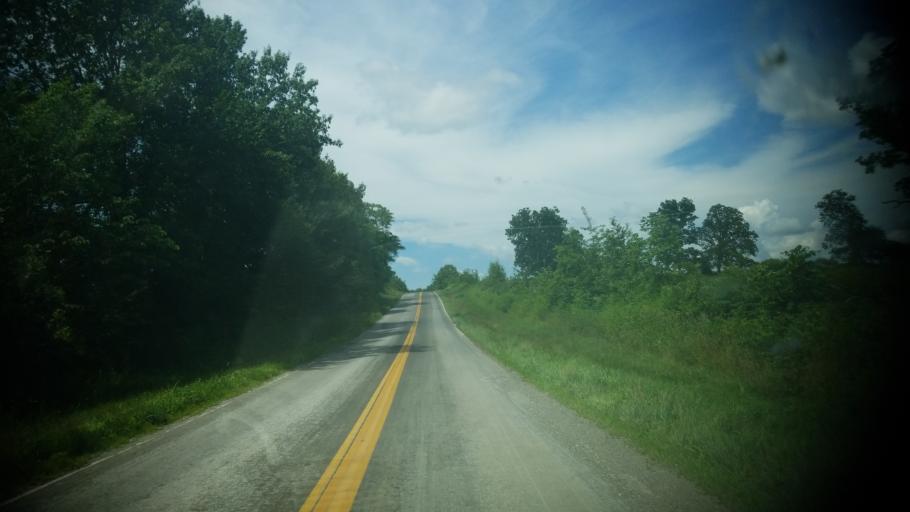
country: US
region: Missouri
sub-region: Audrain County
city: Vandalia
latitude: 39.3120
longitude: -91.3450
